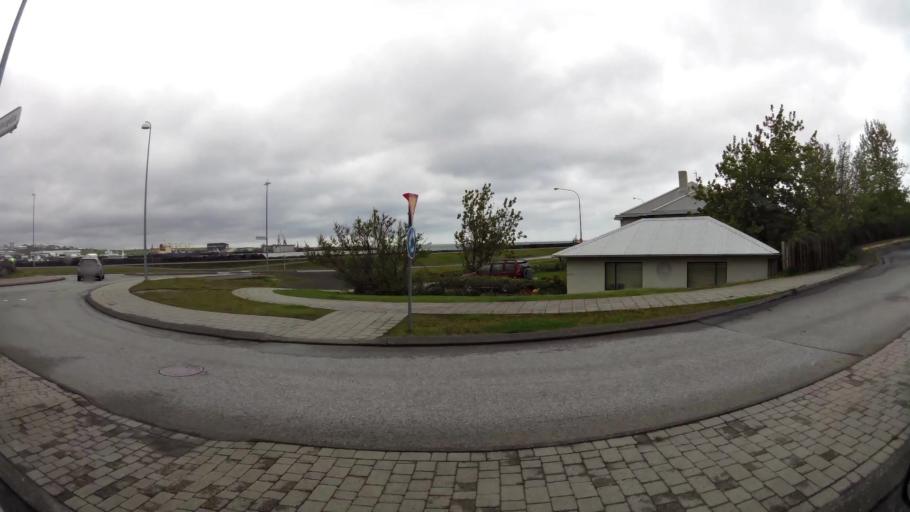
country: IS
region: Capital Region
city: Hafnarfjoerdur
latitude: 64.0720
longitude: -21.9662
